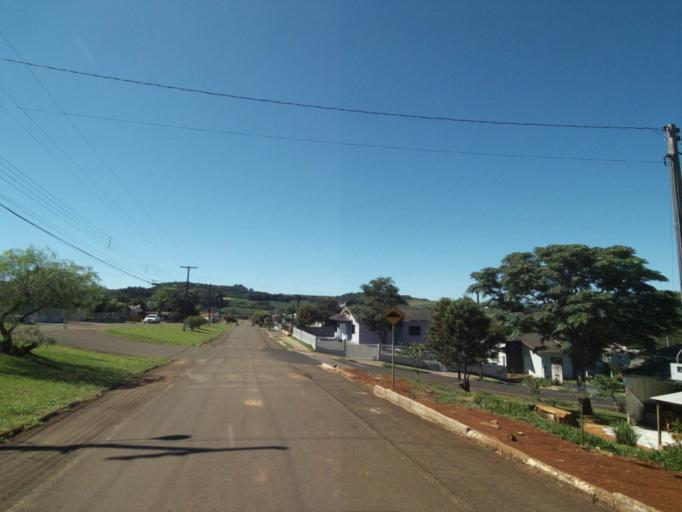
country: BR
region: Santa Catarina
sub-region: Sao Lourenco Do Oeste
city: Sao Lourenco dOeste
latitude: -26.2694
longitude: -52.7816
